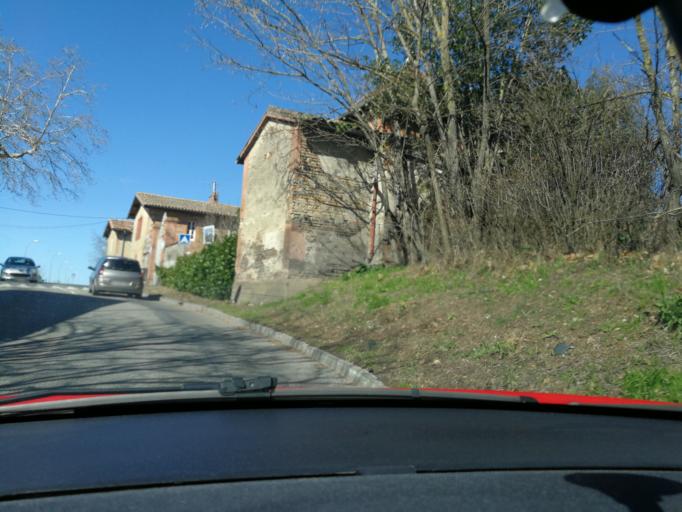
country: FR
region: Midi-Pyrenees
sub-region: Departement de la Haute-Garonne
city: Portet-sur-Garonne
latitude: 43.5434
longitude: 1.3892
